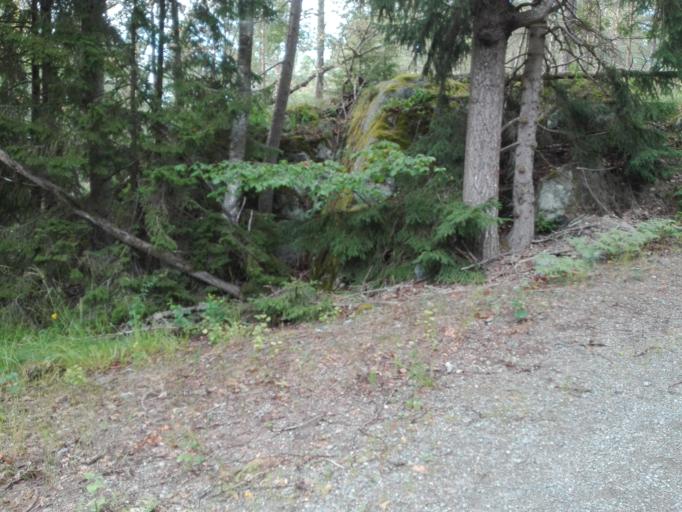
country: SE
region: Stockholm
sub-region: Tyreso Kommun
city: Bollmora
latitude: 59.2804
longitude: 18.2261
